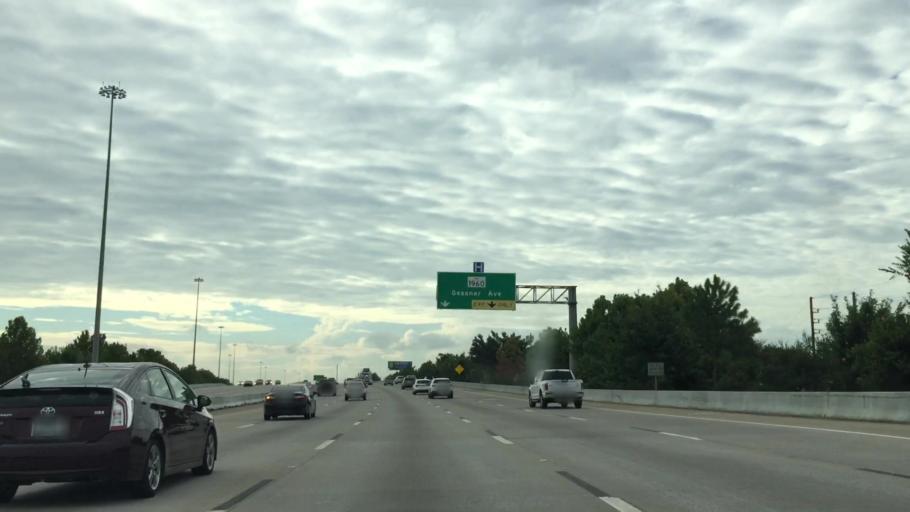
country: US
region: Texas
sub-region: Harris County
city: Oak Cliff Place
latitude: 29.9697
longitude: -95.5604
